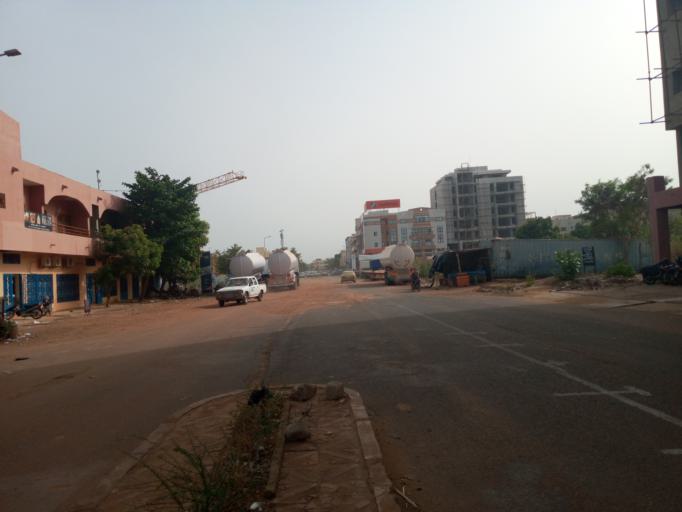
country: ML
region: Bamako
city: Bamako
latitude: 12.6286
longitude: -8.0290
